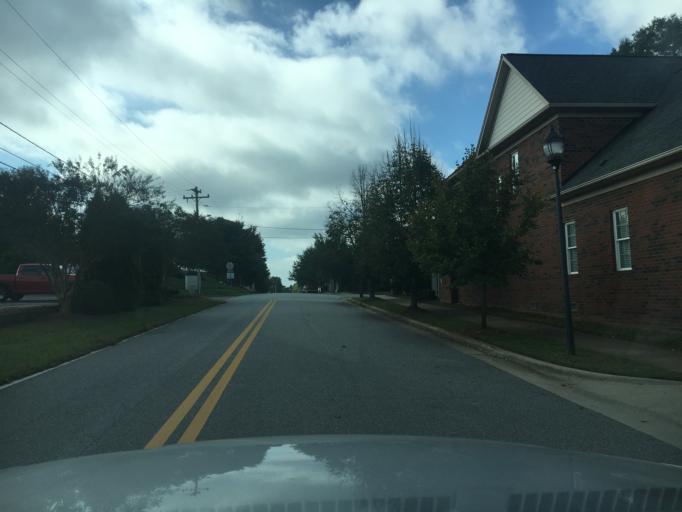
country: US
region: North Carolina
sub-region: Catawba County
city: Hickory
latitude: 35.7517
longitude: -81.3380
